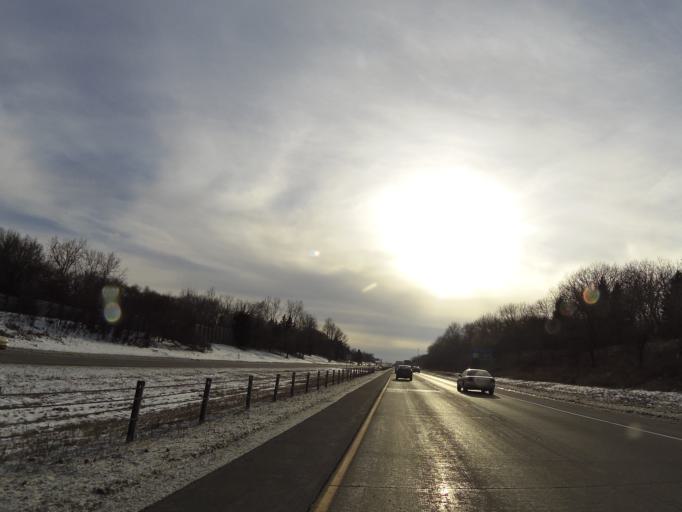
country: US
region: Minnesota
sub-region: Dakota County
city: Apple Valley
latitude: 44.7693
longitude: -93.2320
